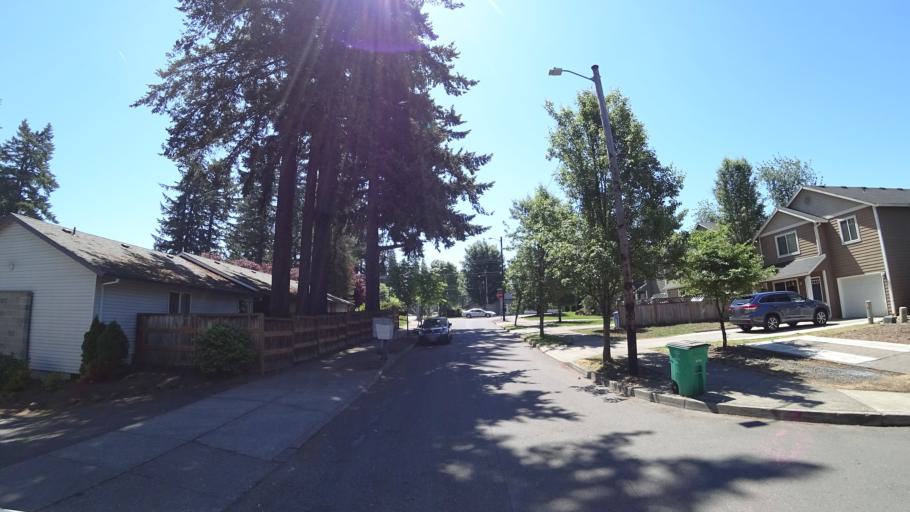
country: US
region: Oregon
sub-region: Clackamas County
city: Happy Valley
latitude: 45.4774
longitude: -122.5263
